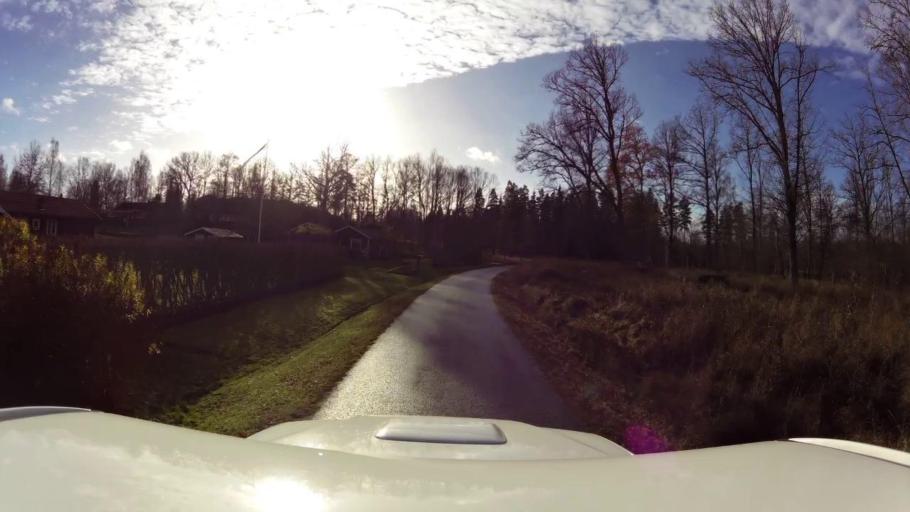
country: SE
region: OEstergoetland
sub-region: Linkopings Kommun
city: Sturefors
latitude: 58.2597
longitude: 15.6960
